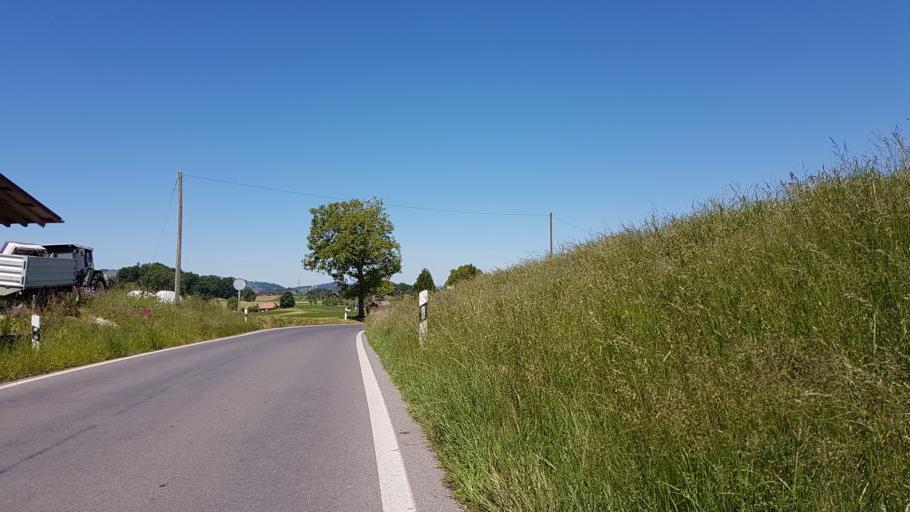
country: CH
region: Bern
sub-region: Thun District
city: Thierachern
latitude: 46.7395
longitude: 7.5606
